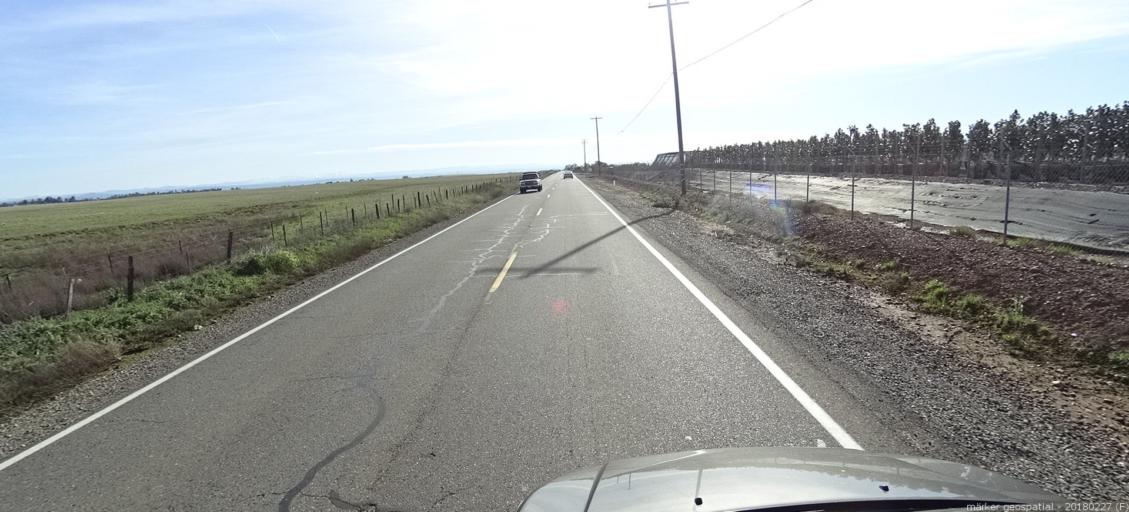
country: US
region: California
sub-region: Sacramento County
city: Vineyard
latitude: 38.4962
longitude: -121.2956
